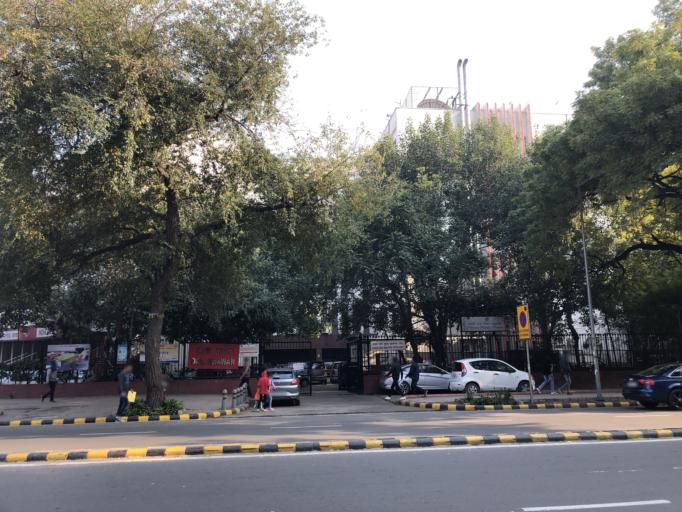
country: IN
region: NCT
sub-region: New Delhi
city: New Delhi
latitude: 28.6229
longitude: 77.2123
